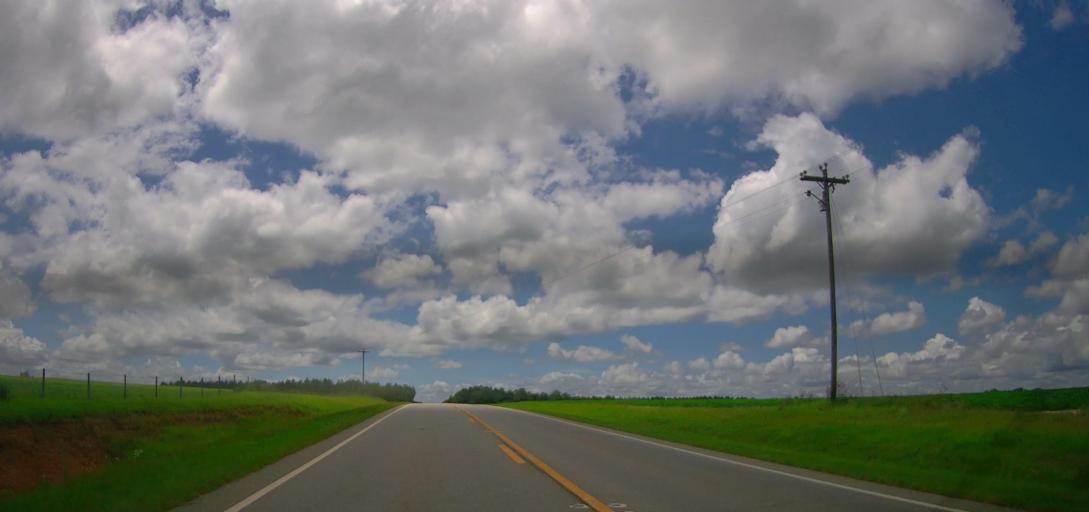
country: US
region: Georgia
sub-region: Turner County
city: Ashburn
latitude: 31.7218
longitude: -83.5150
